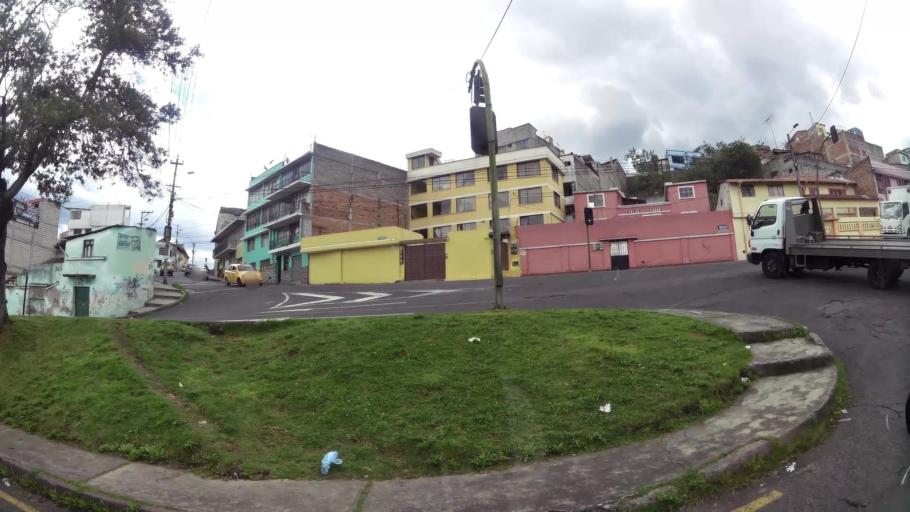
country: EC
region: Pichincha
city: Quito
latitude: -0.2502
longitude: -78.5147
